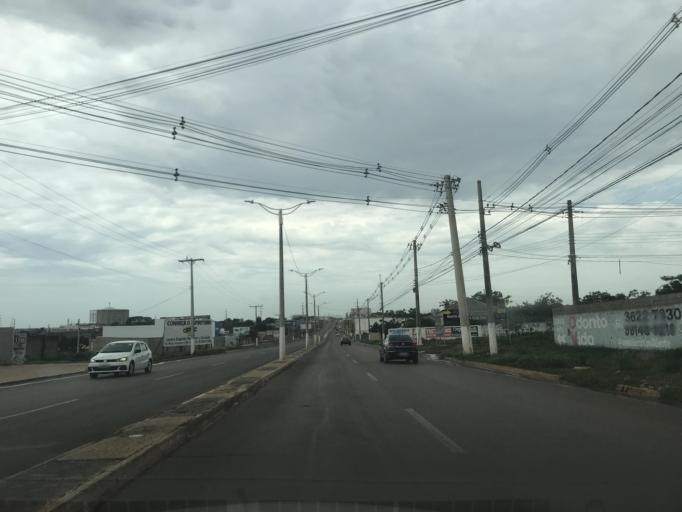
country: BR
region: Goias
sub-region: Luziania
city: Luziania
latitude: -16.2290
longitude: -47.9391
